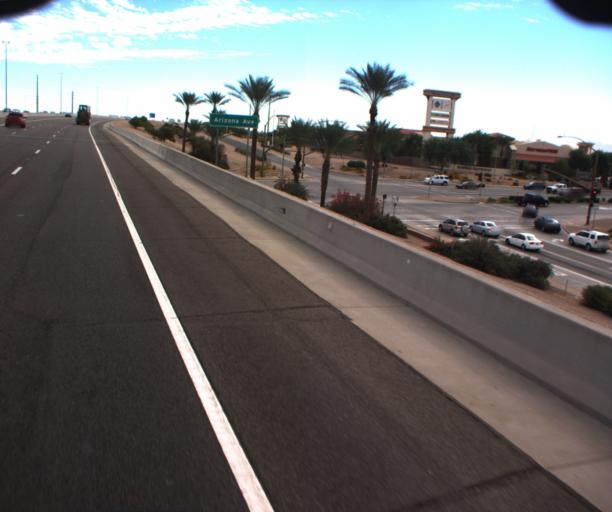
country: US
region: Arizona
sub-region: Maricopa County
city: Chandler
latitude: 33.2872
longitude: -111.8423
